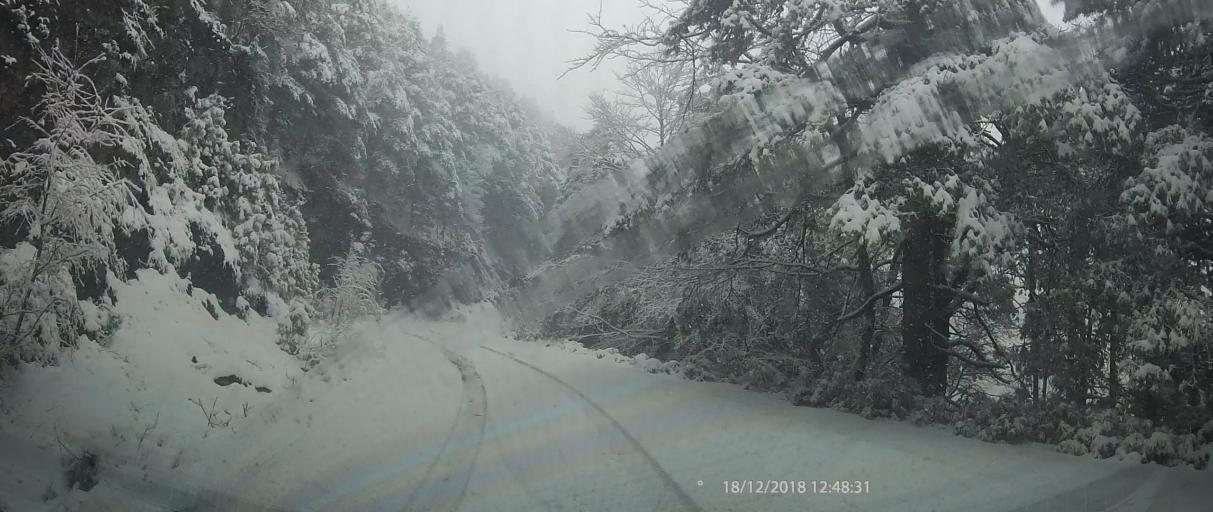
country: GR
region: Central Macedonia
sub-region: Nomos Pierias
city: Litochoro
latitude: 40.1024
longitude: 22.4388
